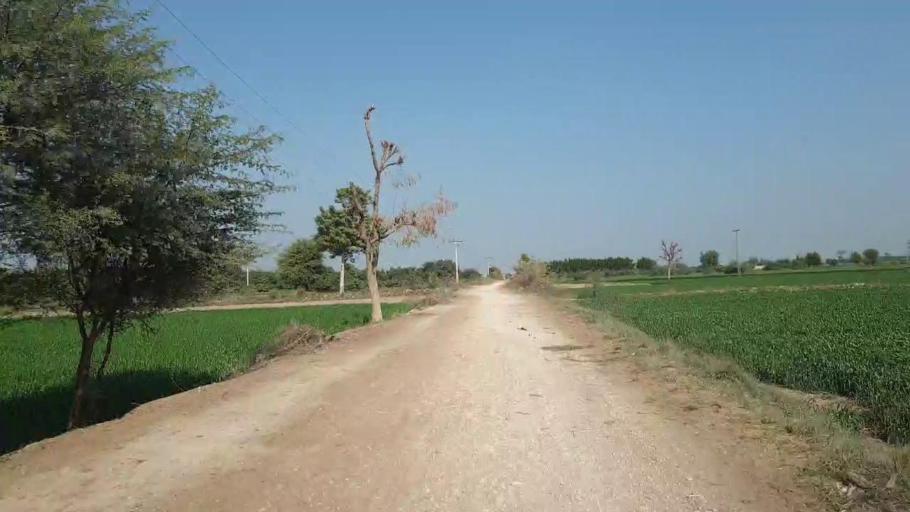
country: PK
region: Sindh
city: Hala
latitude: 25.9120
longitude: 68.4298
